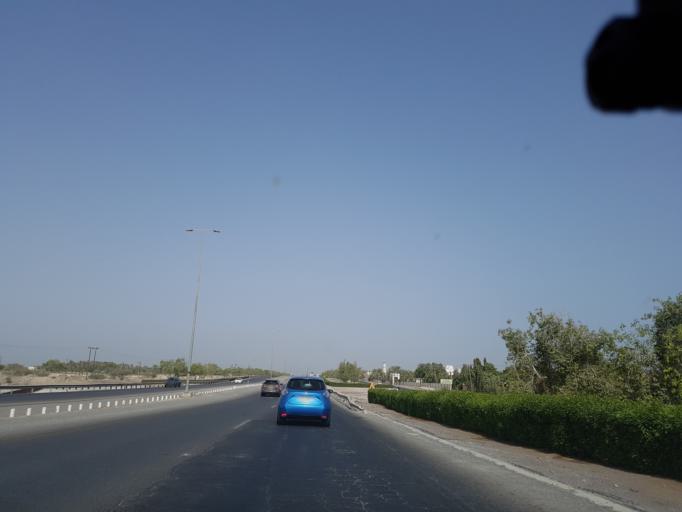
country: OM
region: Al Batinah
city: Barka'
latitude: 23.7295
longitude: 57.7076
